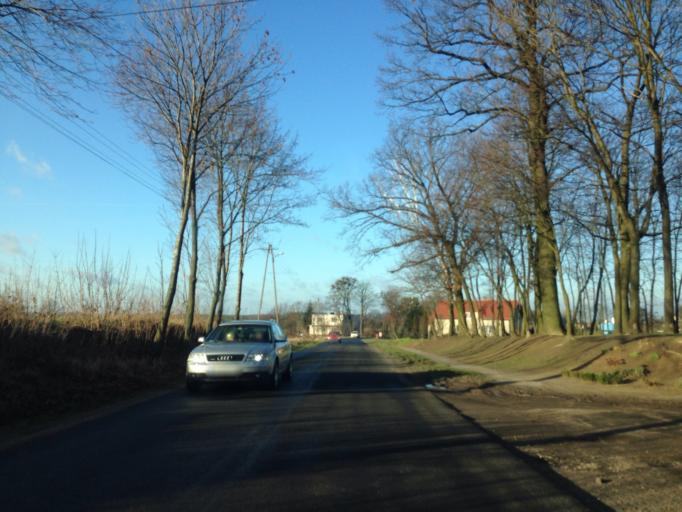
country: PL
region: Kujawsko-Pomorskie
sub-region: Powiat brodnicki
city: Jablonowo Pomorskie
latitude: 53.3988
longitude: 19.1483
